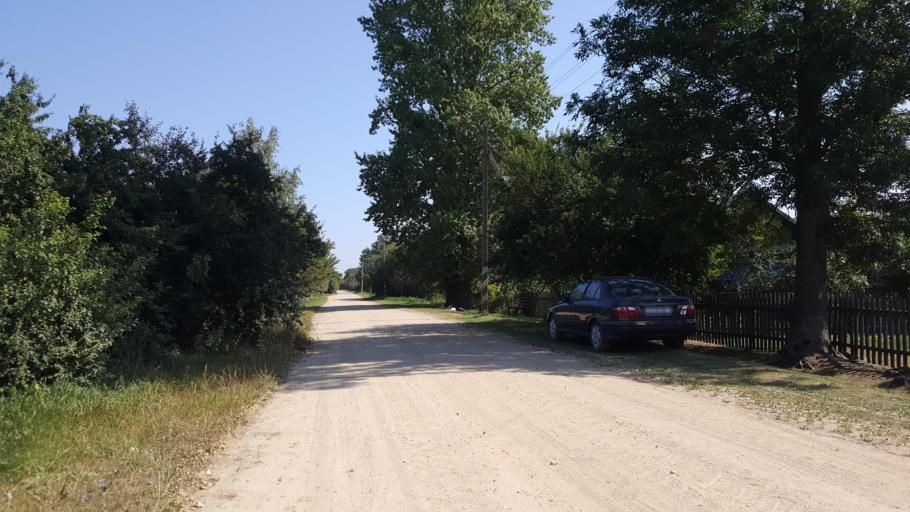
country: PL
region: Podlasie
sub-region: Powiat hajnowski
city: Czeremcha
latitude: 52.4677
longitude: 23.4554
